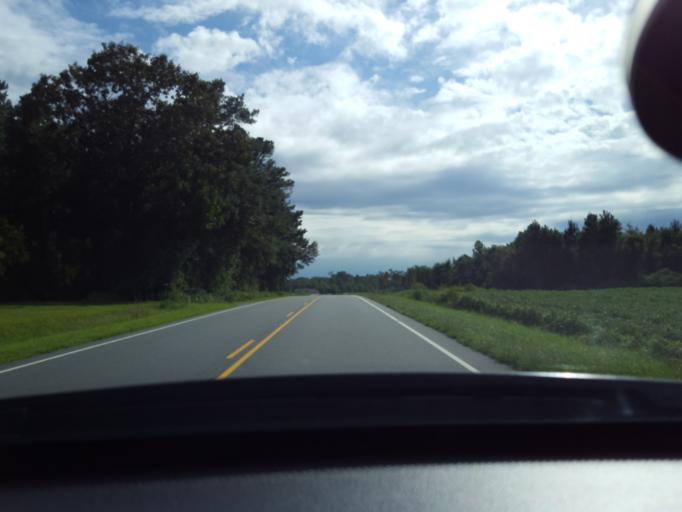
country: US
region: North Carolina
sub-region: Duplin County
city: Kenansville
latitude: 34.9974
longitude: -77.9210
